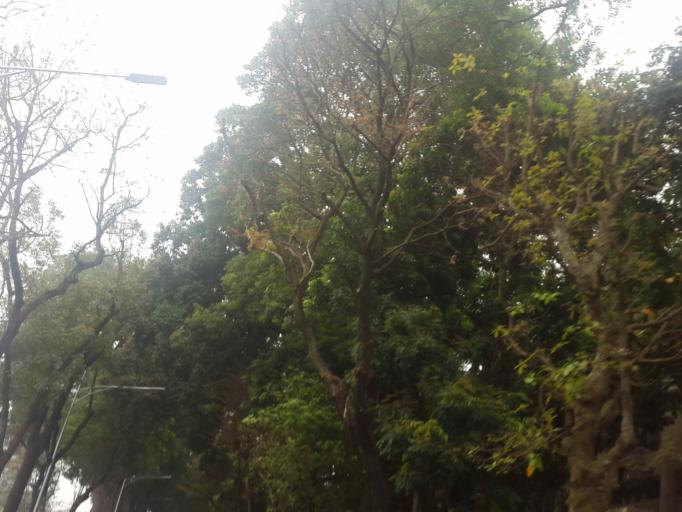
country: VN
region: Ha Noi
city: Hoan Kiem
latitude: 21.0302
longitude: 105.8511
